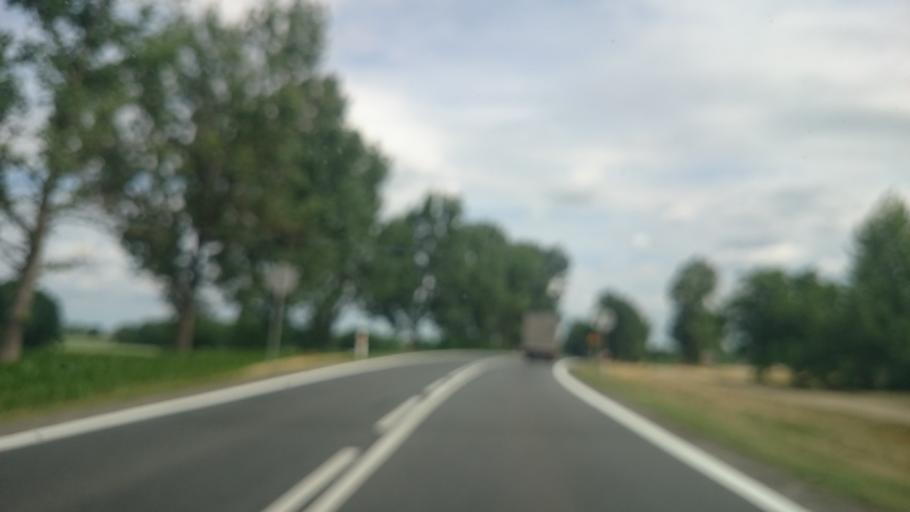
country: PL
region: Lower Silesian Voivodeship
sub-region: Powiat wroclawski
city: Kobierzyce
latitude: 50.9293
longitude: 16.8974
